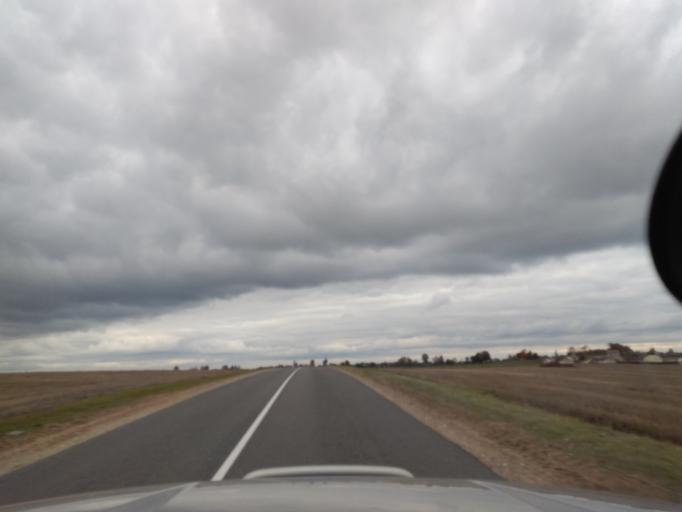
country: BY
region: Minsk
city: Slutsk
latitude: 53.1969
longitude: 27.3576
